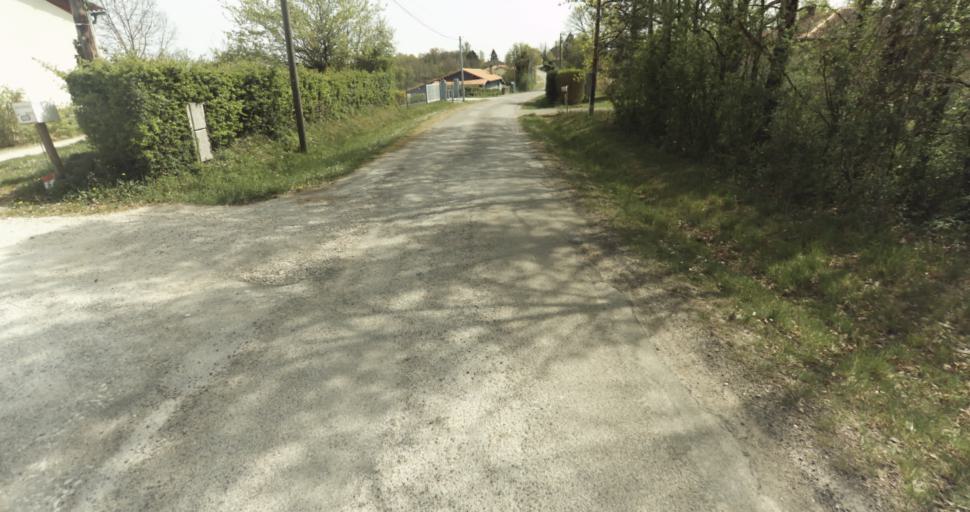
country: FR
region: Midi-Pyrenees
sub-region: Departement du Tarn-et-Garonne
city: Moissac
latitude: 44.1605
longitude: 1.0770
